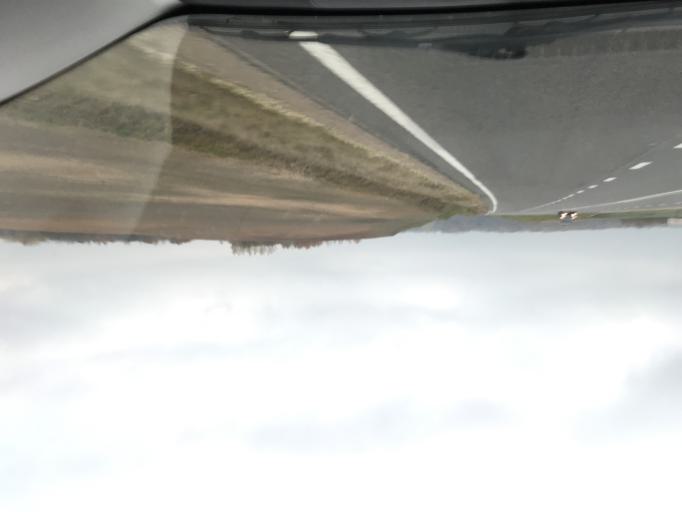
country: BY
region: Vitebsk
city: Vitebsk
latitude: 55.1584
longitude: 30.0656
